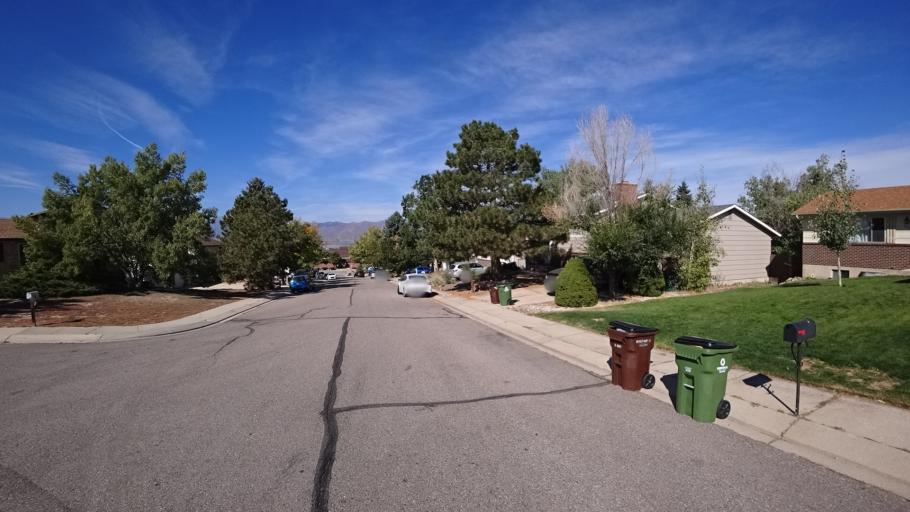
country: US
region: Colorado
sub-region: El Paso County
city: Cimarron Hills
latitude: 38.9201
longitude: -104.7677
